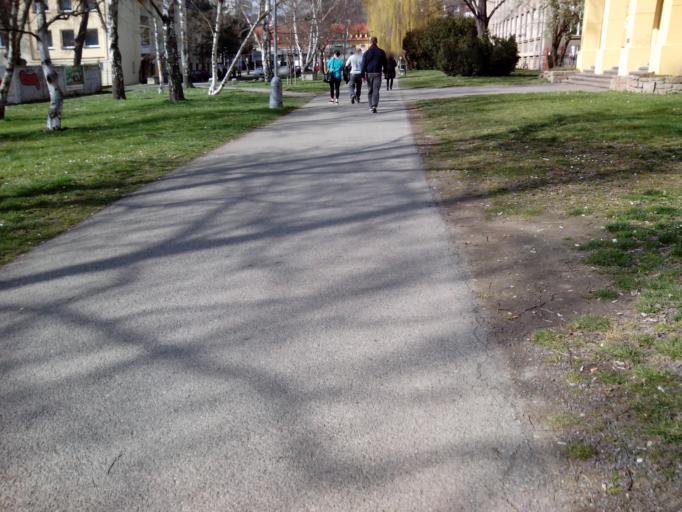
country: CZ
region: Central Bohemia
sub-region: Okres Beroun
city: Beroun
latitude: 49.9603
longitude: 14.0747
